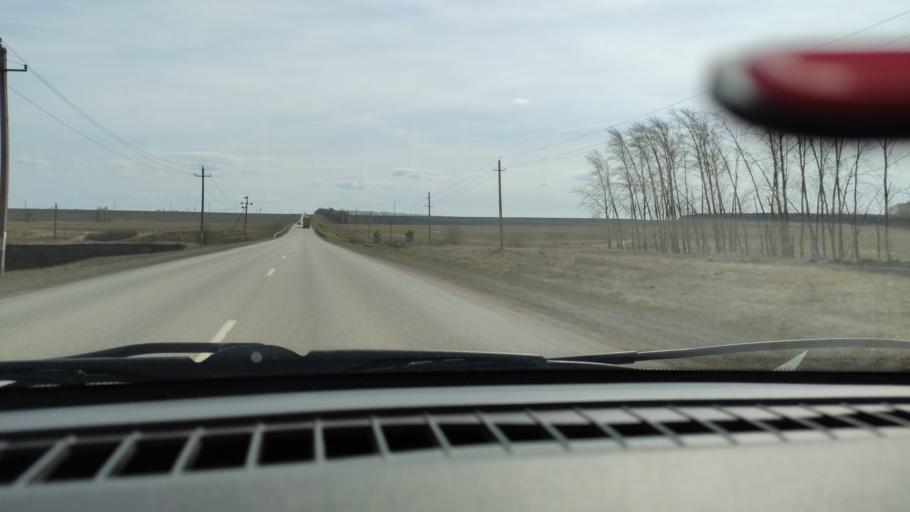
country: RU
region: Bashkortostan
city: Dyurtyuli
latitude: 55.3475
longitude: 54.9251
